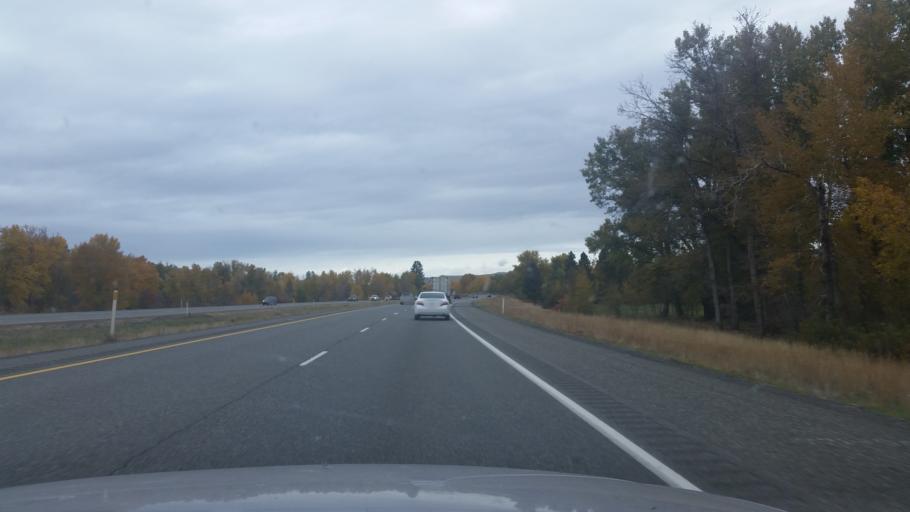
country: US
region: Washington
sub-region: Kittitas County
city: Ellensburg
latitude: 47.0335
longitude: -120.6242
